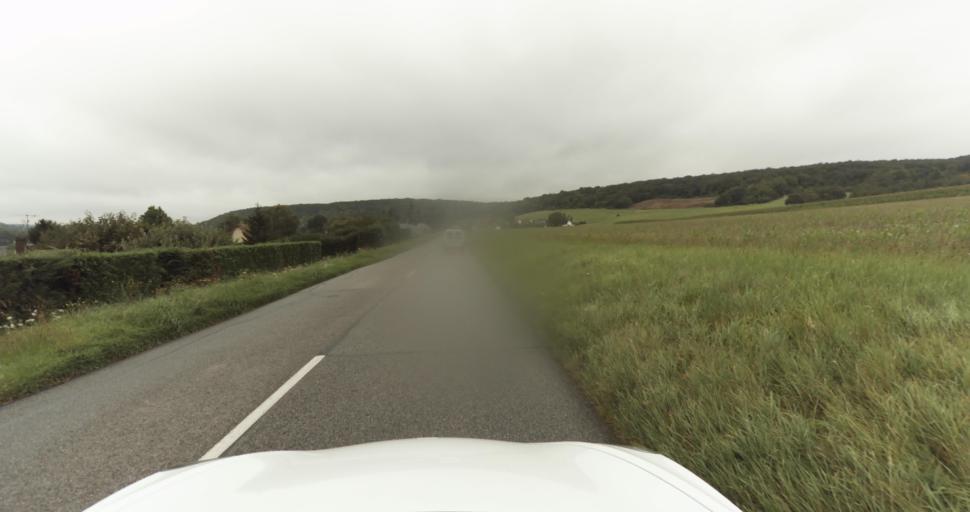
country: FR
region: Haute-Normandie
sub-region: Departement de l'Eure
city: Normanville
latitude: 49.0751
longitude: 1.1667
